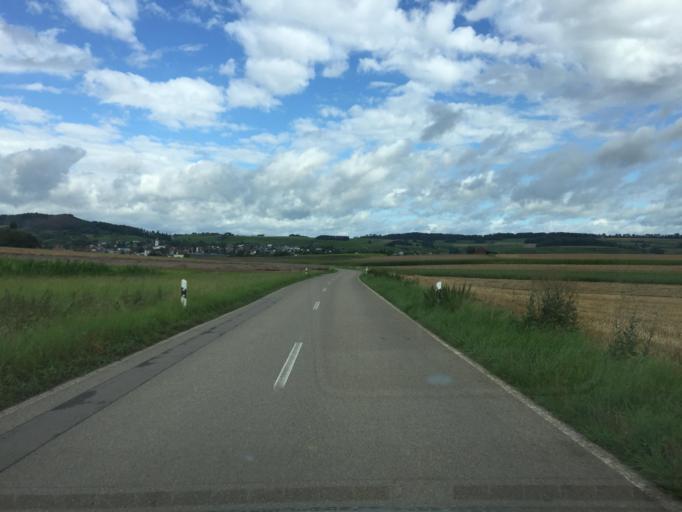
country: CH
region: Schaffhausen
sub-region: Bezirk Unterklettgau
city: Wilchingen
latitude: 47.6542
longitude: 8.4443
